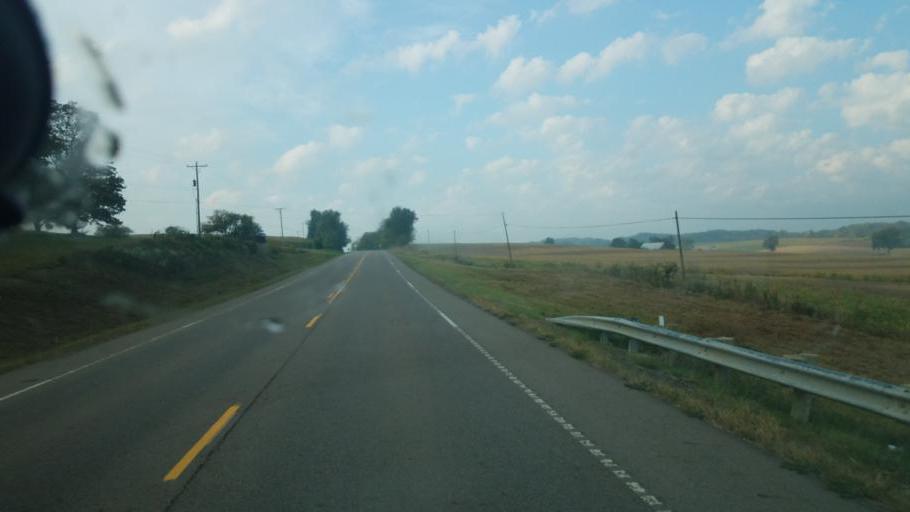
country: US
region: Ohio
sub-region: Licking County
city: Utica
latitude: 40.2568
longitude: -82.4059
